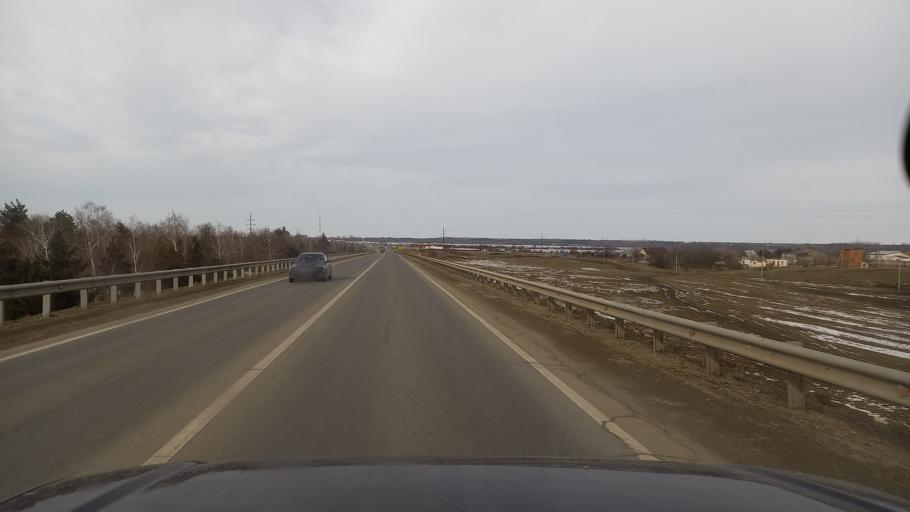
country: RU
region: Krasnodarskiy
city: Belorechensk
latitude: 44.7630
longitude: 39.9146
